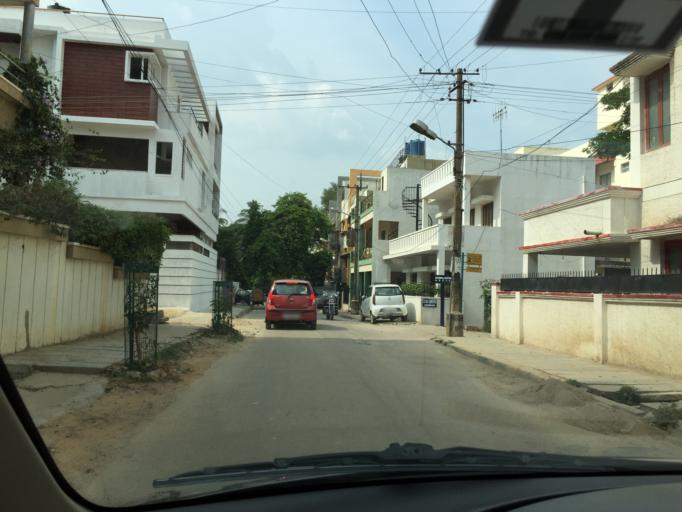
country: IN
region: Karnataka
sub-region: Bangalore Urban
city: Bangalore
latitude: 13.0044
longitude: 77.6248
